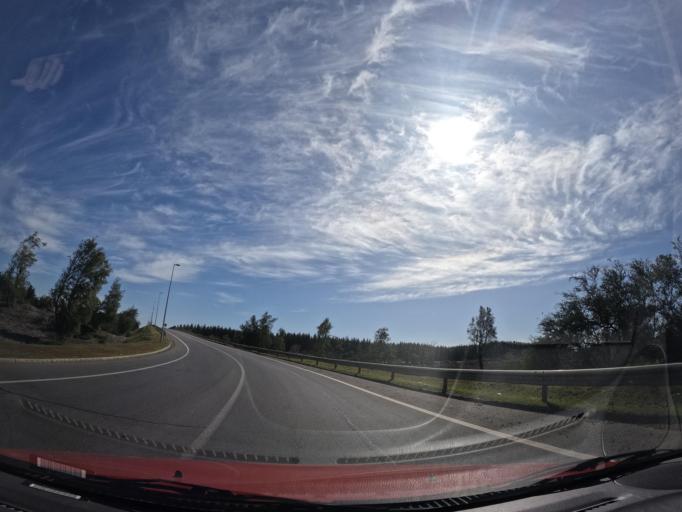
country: CL
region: Biobio
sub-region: Provincia de Biobio
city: Cabrero
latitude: -36.9352
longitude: -72.3495
